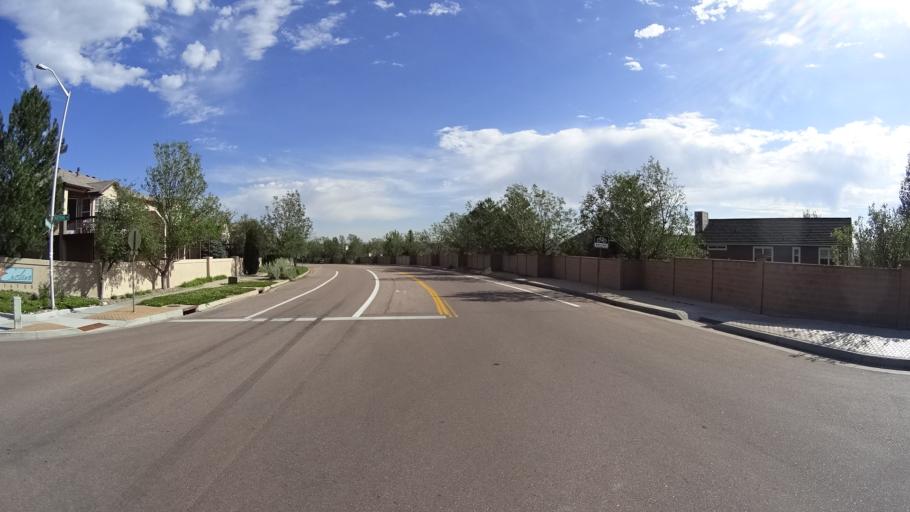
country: US
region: Colorado
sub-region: El Paso County
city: Fort Carson
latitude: 38.7621
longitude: -104.8188
